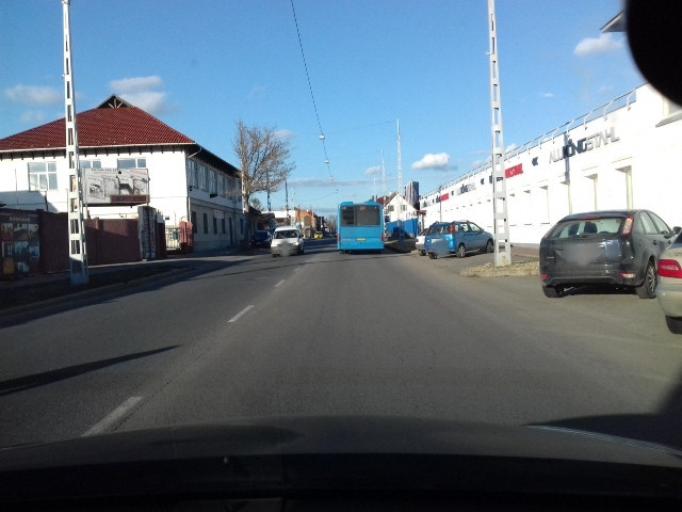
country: HU
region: Budapest
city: Budapest IV. keruelet
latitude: 47.5740
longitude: 19.0897
